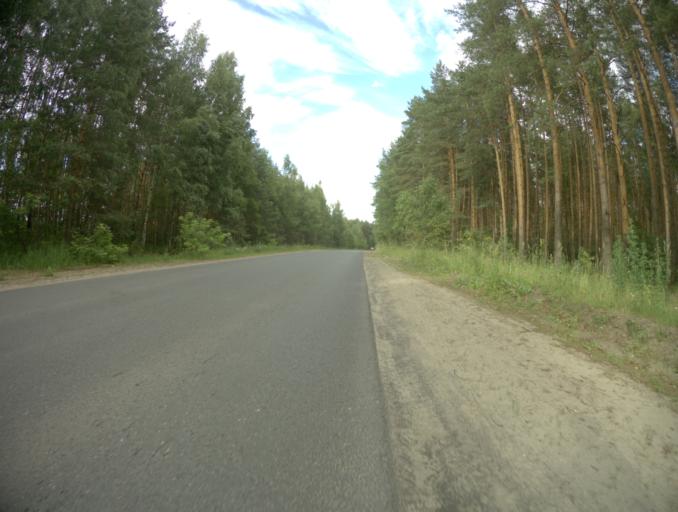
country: RU
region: Vladimir
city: Kommunar
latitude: 56.1284
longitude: 40.4838
